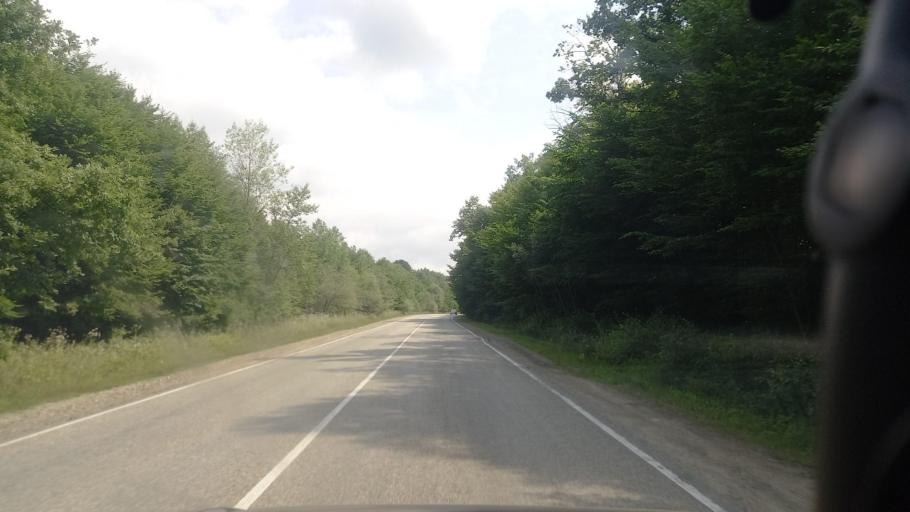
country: RU
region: Karachayevo-Cherkesiya
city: Kurdzhinovo
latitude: 44.0365
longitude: 40.8969
